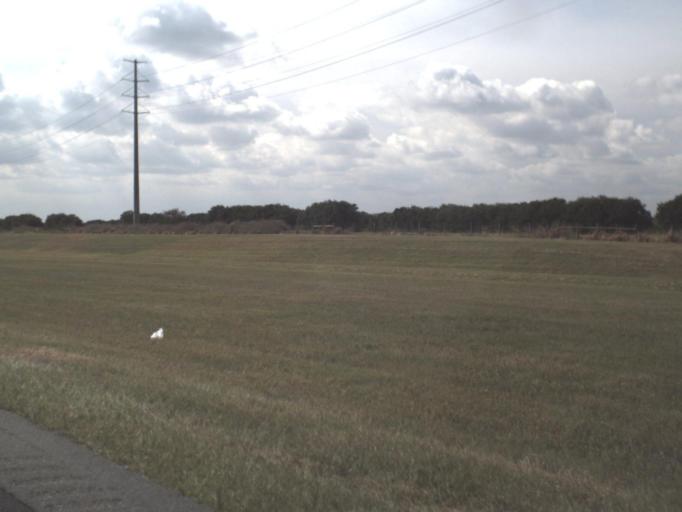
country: US
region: Florida
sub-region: Polk County
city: Fussels Corner
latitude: 28.0926
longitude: -81.8300
